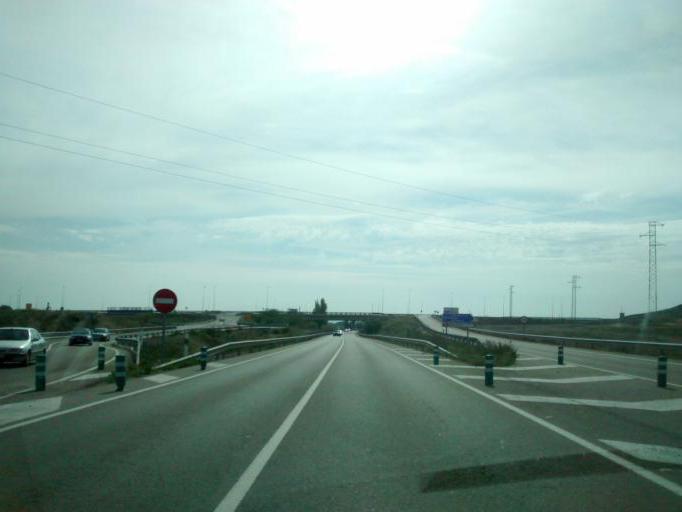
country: ES
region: Aragon
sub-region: Provincia de Zaragoza
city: El Burgo de Ebro
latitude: 41.5461
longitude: -0.7000
